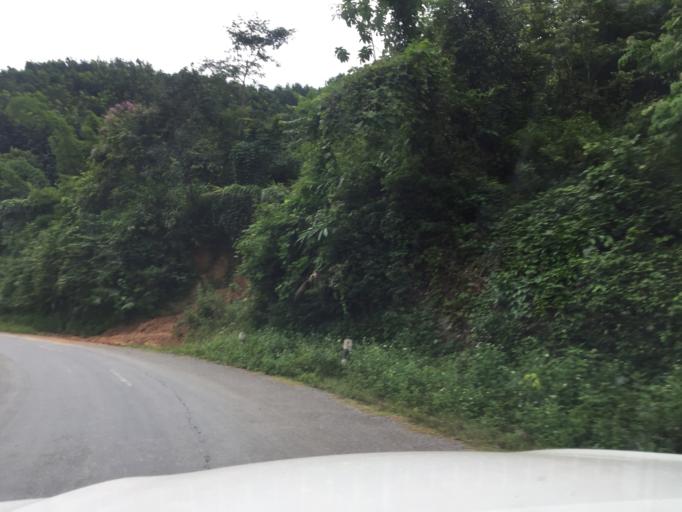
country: LA
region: Oudomxai
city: Muang La
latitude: 21.1072
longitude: 102.2324
